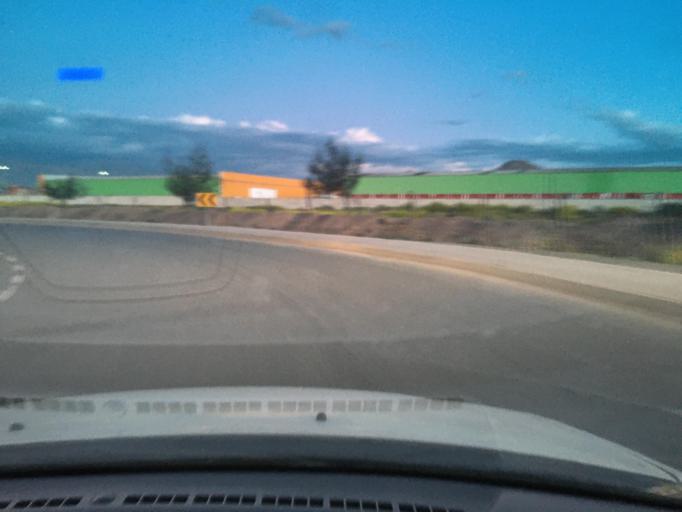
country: CL
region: Santiago Metropolitan
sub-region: Provincia de Chacabuco
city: Chicureo Abajo
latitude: -33.2916
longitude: -70.7371
